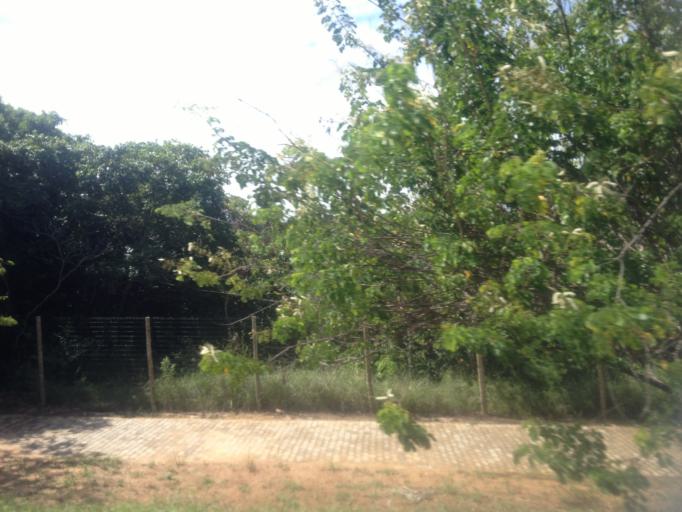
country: BR
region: Bahia
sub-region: Mata De Sao Joao
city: Mata de Sao Joao
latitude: -12.5676
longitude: -38.0171
